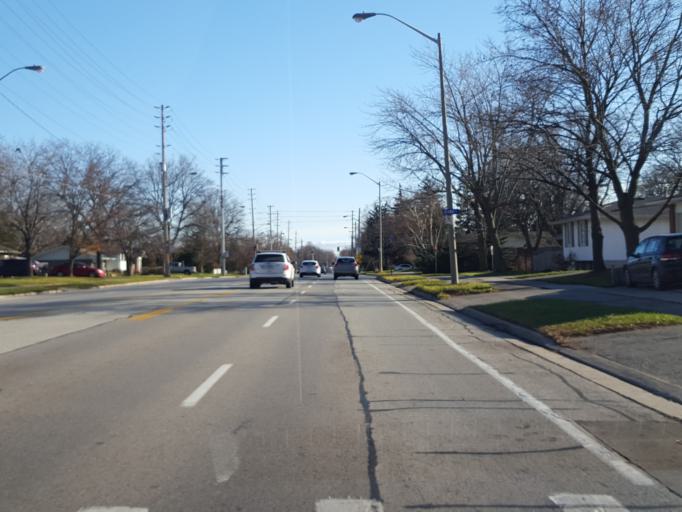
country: CA
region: Ontario
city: Burlington
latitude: 43.3567
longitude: -79.7745
